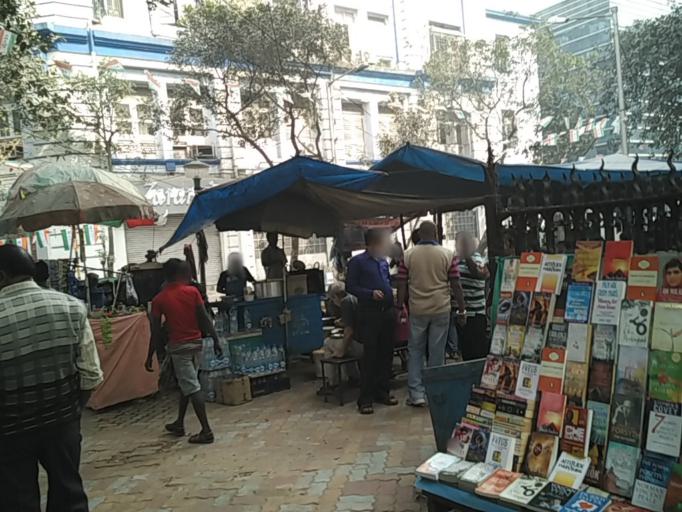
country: IN
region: West Bengal
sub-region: Kolkata
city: Bara Bazar
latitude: 22.5584
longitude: 88.3507
